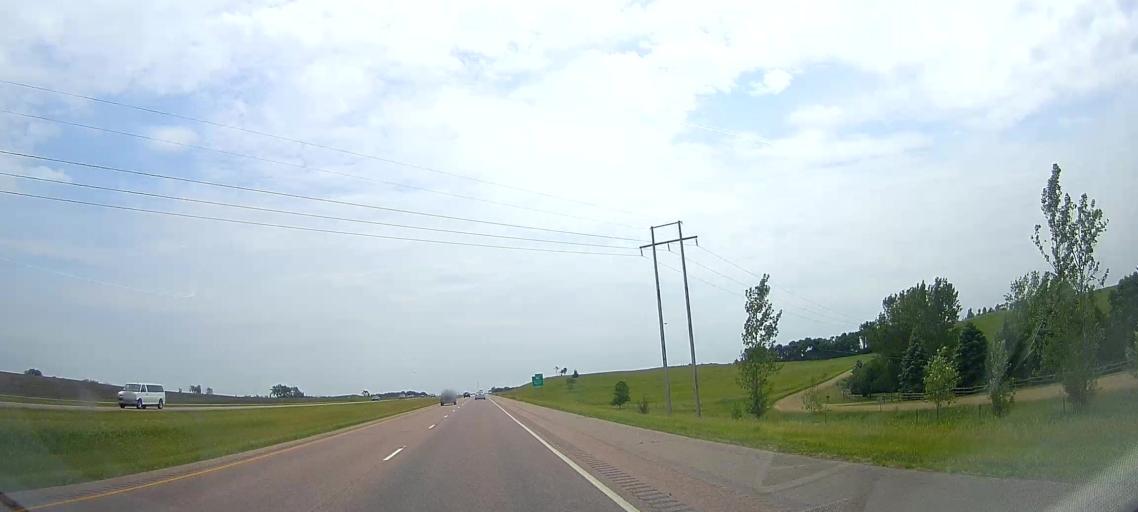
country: US
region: South Dakota
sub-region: Minnehaha County
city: Hartford
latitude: 43.6589
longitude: -97.1095
